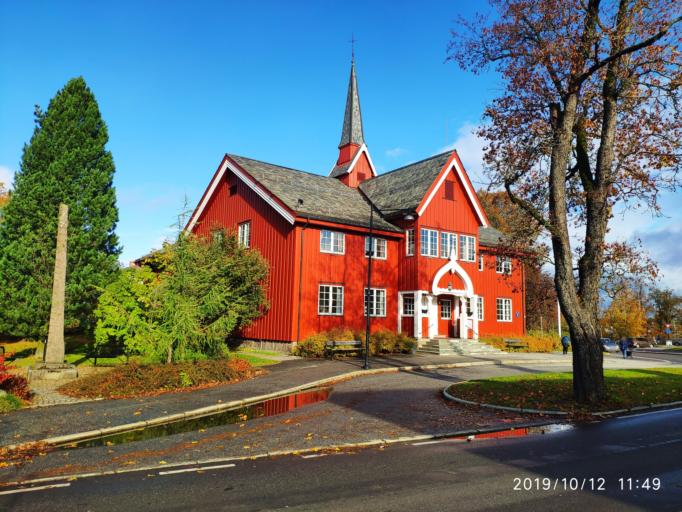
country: NO
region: Akershus
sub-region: Ullensaker
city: Jessheim
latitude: 60.1406
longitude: 11.1745
